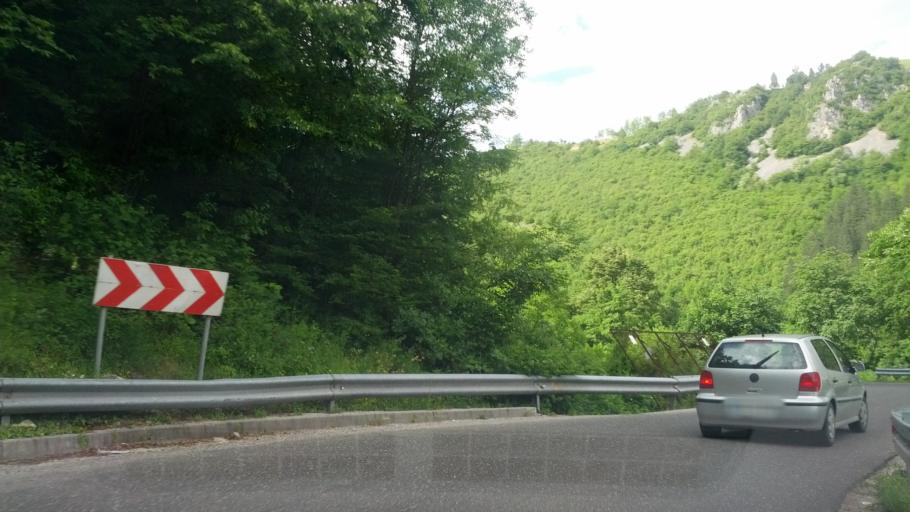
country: BA
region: Federation of Bosnia and Herzegovina
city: Stijena
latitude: 44.9087
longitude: 15.9909
